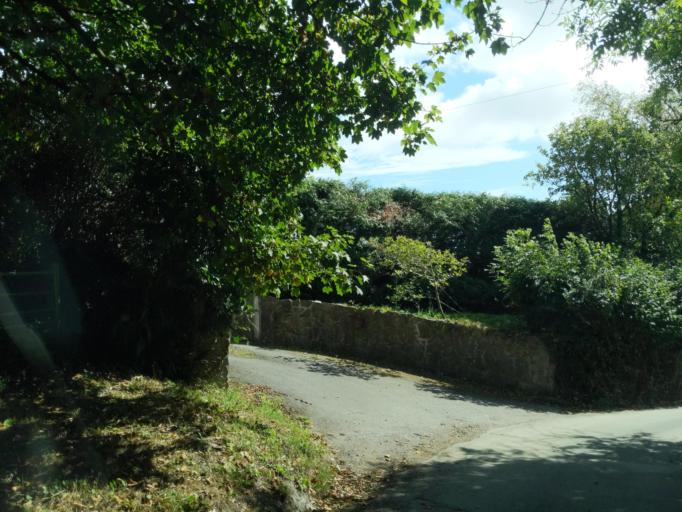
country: GB
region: England
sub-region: Devon
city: Ivybridge
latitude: 50.3746
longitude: -3.9041
